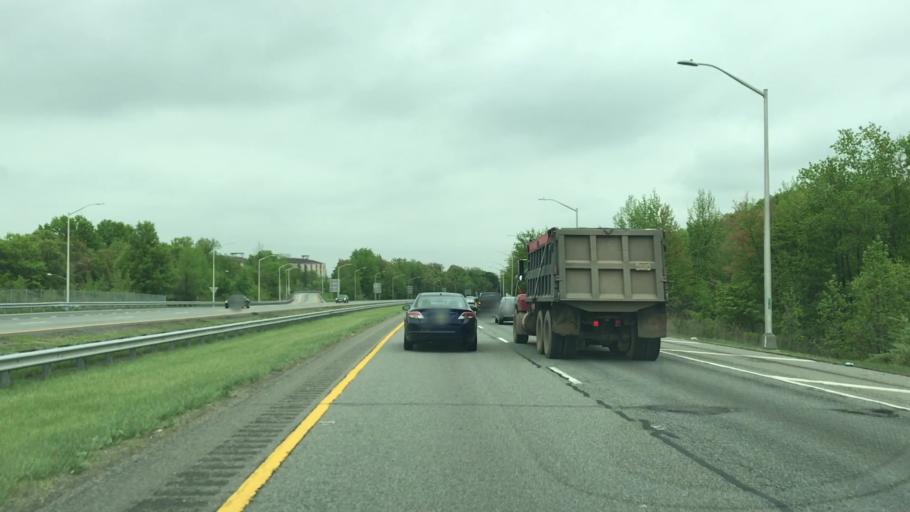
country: US
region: New Jersey
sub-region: Middlesex County
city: Carteret
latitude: 40.5430
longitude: -74.2234
